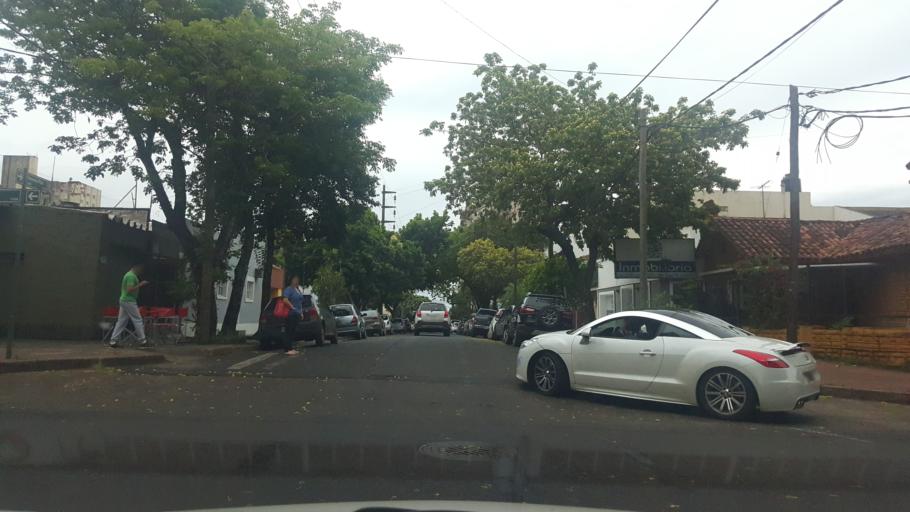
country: AR
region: Misiones
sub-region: Departamento de Capital
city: Posadas
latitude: -27.3676
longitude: -55.8884
